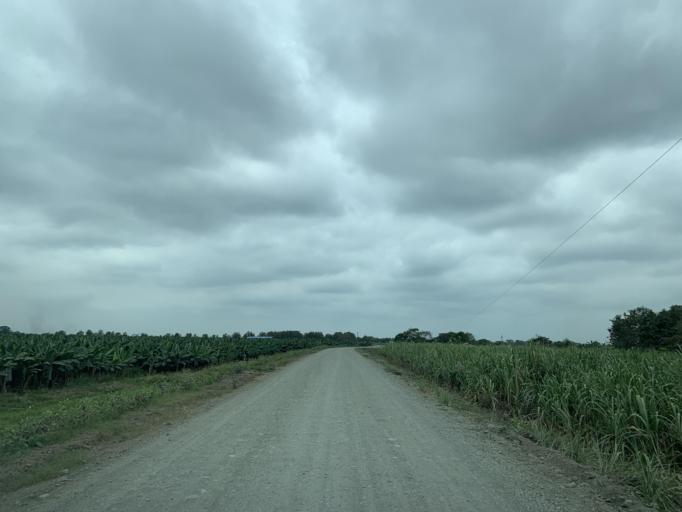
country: EC
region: Guayas
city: Coronel Marcelino Mariduena
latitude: -2.3295
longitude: -79.4542
